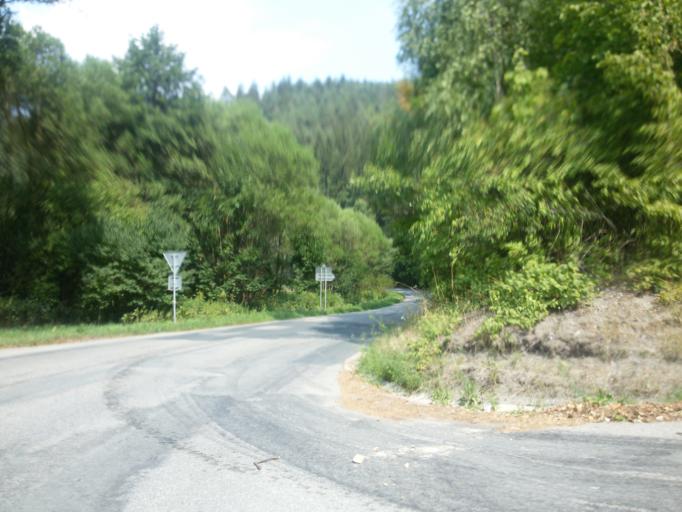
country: CZ
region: South Moravian
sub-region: Okres Brno-Venkov
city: Lomnice
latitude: 49.4135
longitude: 16.4236
